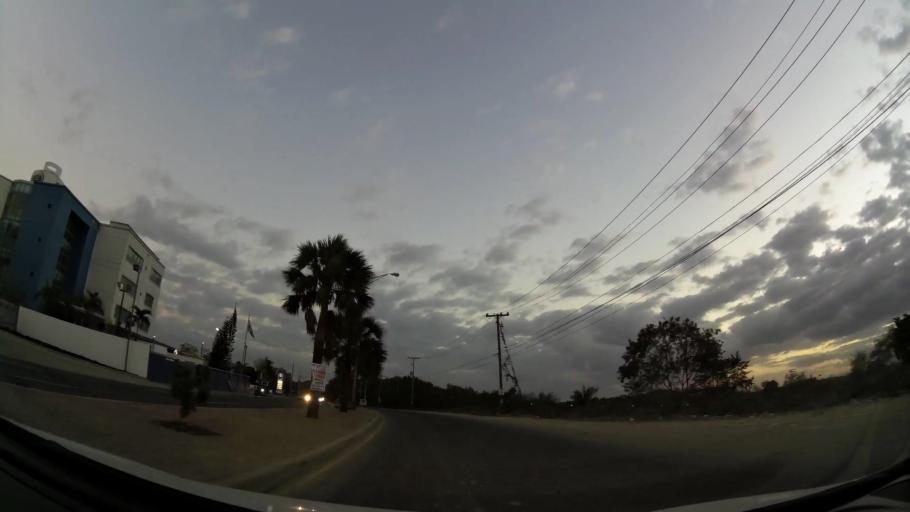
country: DO
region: Nacional
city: La Agustina
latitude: 18.5457
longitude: -69.9535
